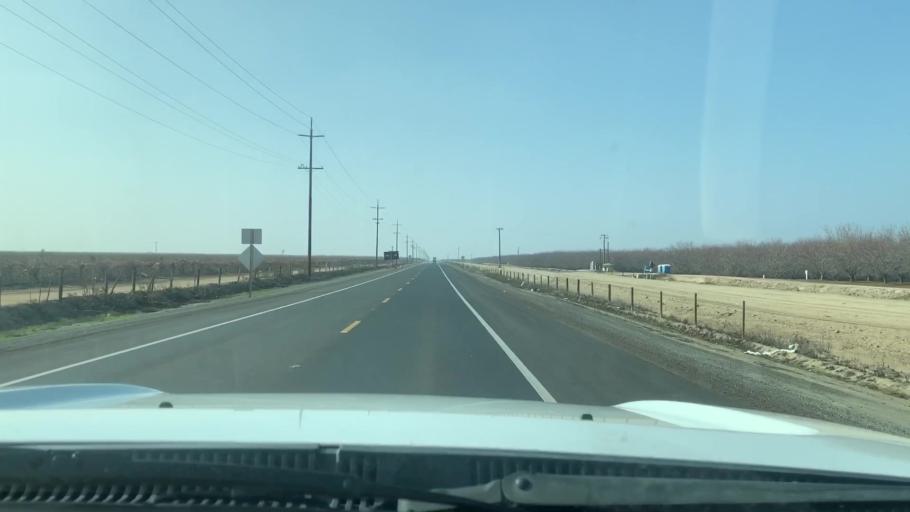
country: US
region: California
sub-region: Kern County
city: McFarland
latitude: 35.6020
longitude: -119.2273
